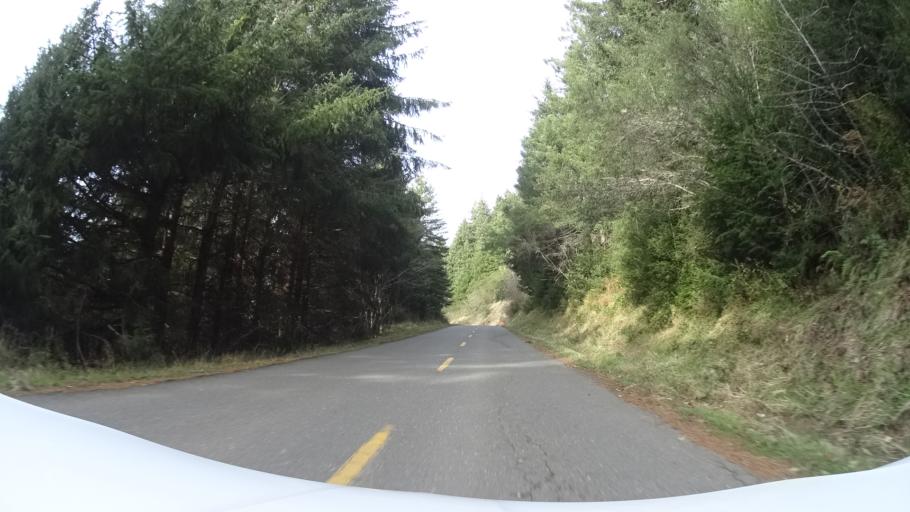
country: US
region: California
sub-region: Humboldt County
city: Ferndale
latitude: 40.5313
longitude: -124.2681
